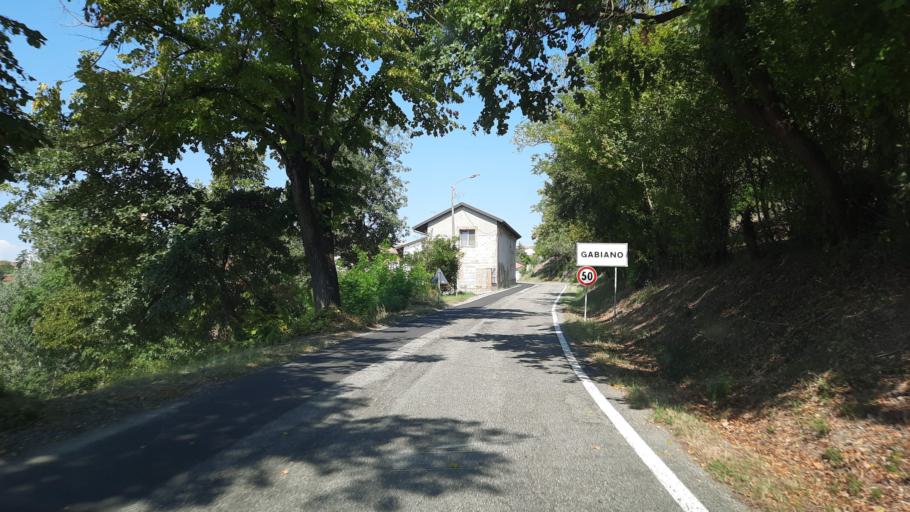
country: IT
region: Piedmont
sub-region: Provincia di Alessandria
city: Gabiano
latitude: 45.1567
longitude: 8.2031
